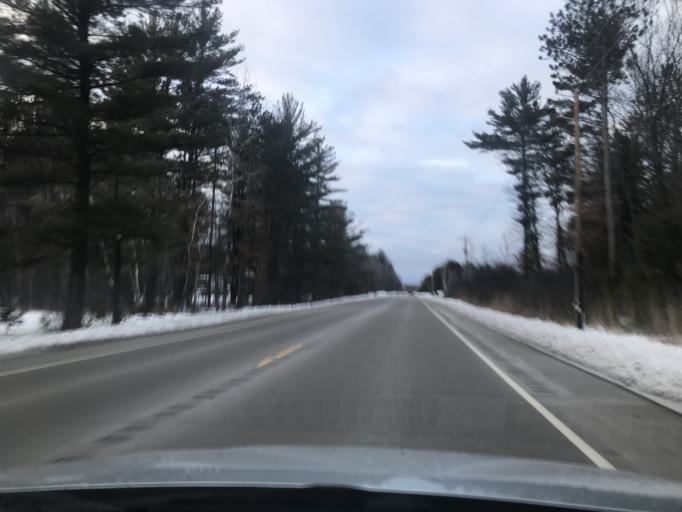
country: US
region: Wisconsin
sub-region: Marinette County
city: Marinette
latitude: 45.1304
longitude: -87.6870
